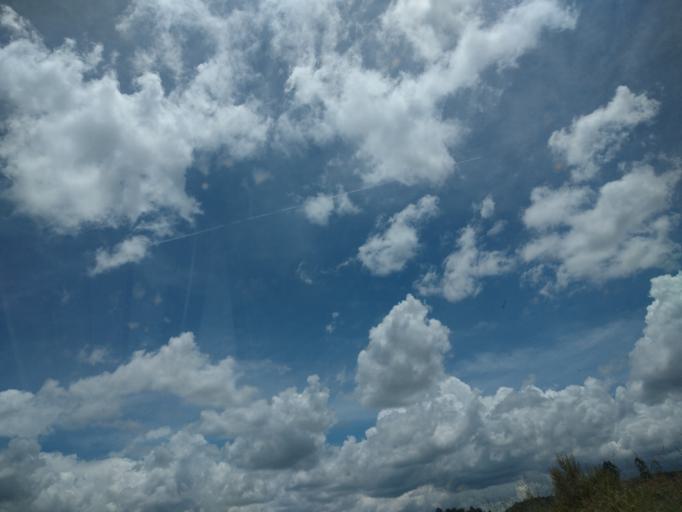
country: BR
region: Minas Gerais
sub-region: Tiradentes
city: Tiradentes
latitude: -20.9087
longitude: -44.2757
